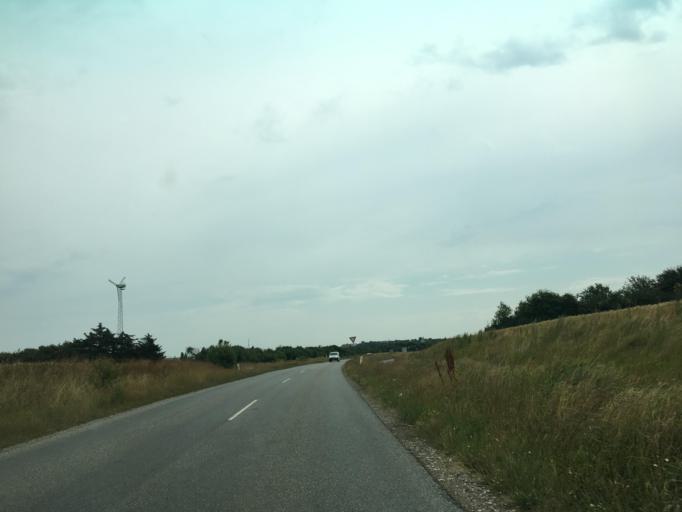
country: DK
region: North Denmark
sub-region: Thisted Kommune
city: Hurup
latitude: 56.7621
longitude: 8.4233
